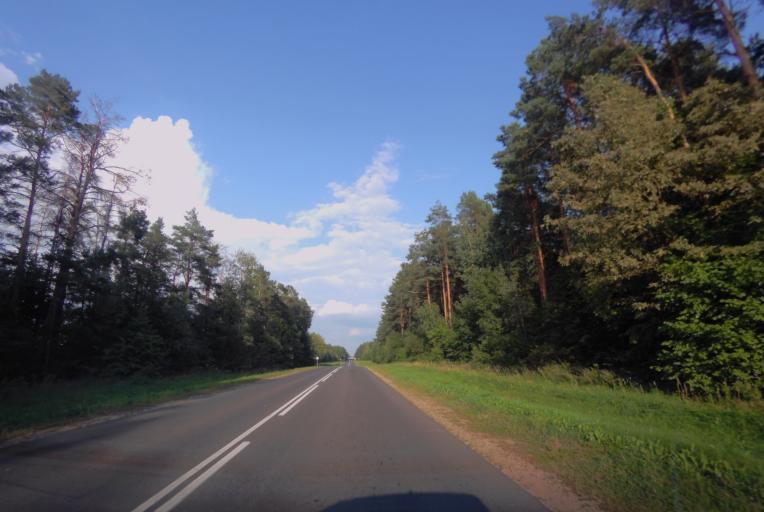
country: BY
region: Minsk
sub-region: Smalyavitski Rayon
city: Oktjabr'skij
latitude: 54.0246
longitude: 28.1907
